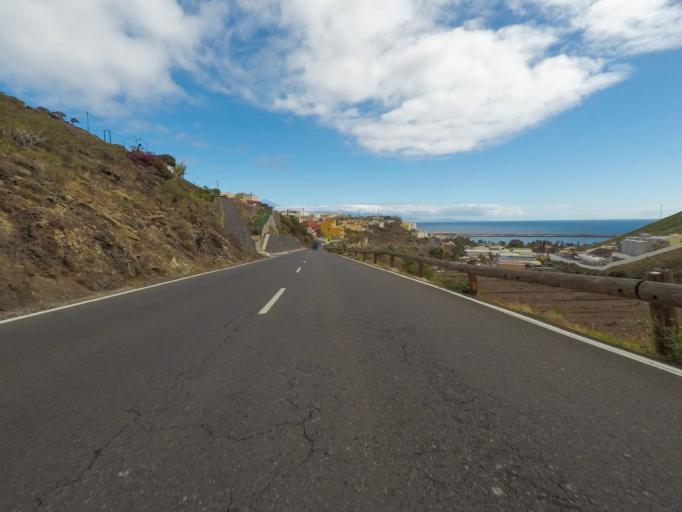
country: ES
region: Canary Islands
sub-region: Provincia de Santa Cruz de Tenerife
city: San Sebastian de la Gomera
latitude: 28.0898
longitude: -17.1216
